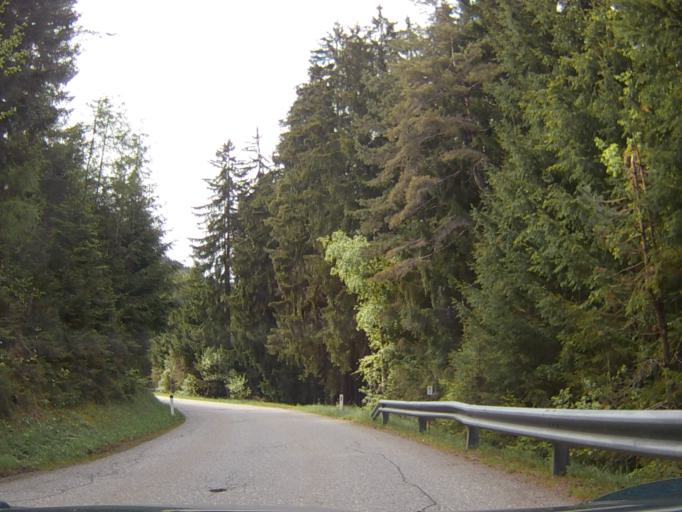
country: AT
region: Carinthia
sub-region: Politischer Bezirk Villach Land
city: Stockenboi
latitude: 46.7347
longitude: 13.5752
